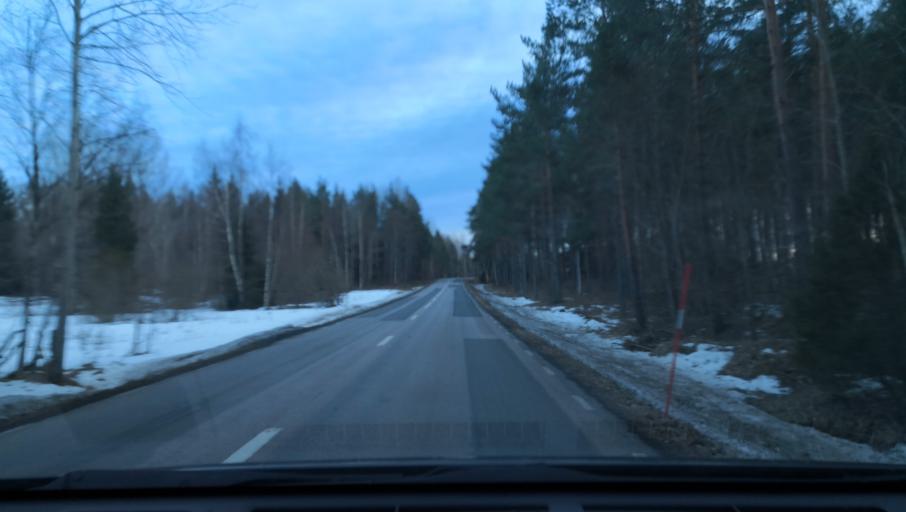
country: SE
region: Uppsala
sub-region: Osthammars Kommun
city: Osterbybruk
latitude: 60.2665
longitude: 17.9555
